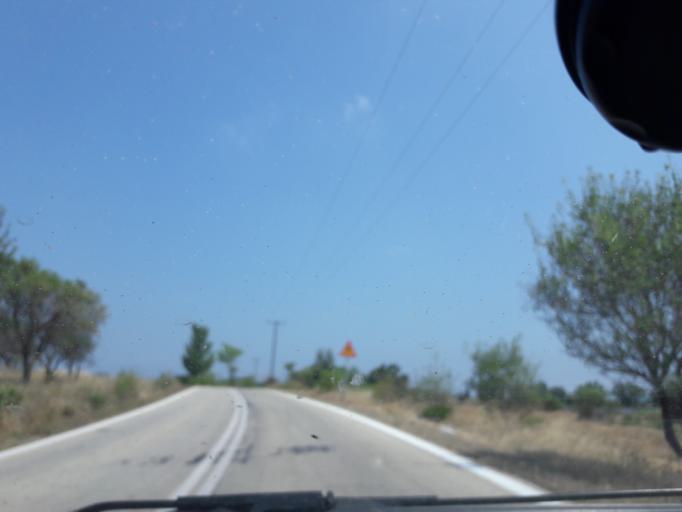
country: GR
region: North Aegean
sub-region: Nomos Lesvou
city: Myrina
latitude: 39.9246
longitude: 25.3265
